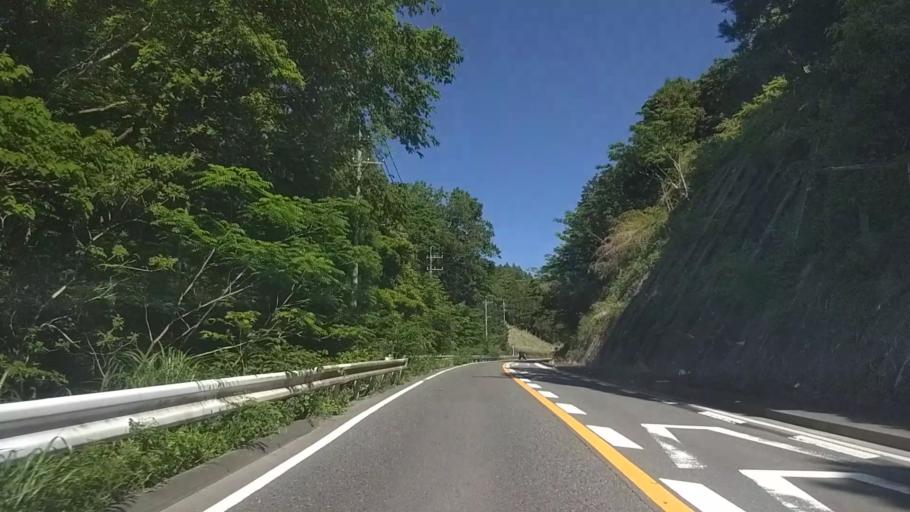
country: JP
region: Shizuoka
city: Fujinomiya
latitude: 35.2692
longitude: 138.4569
